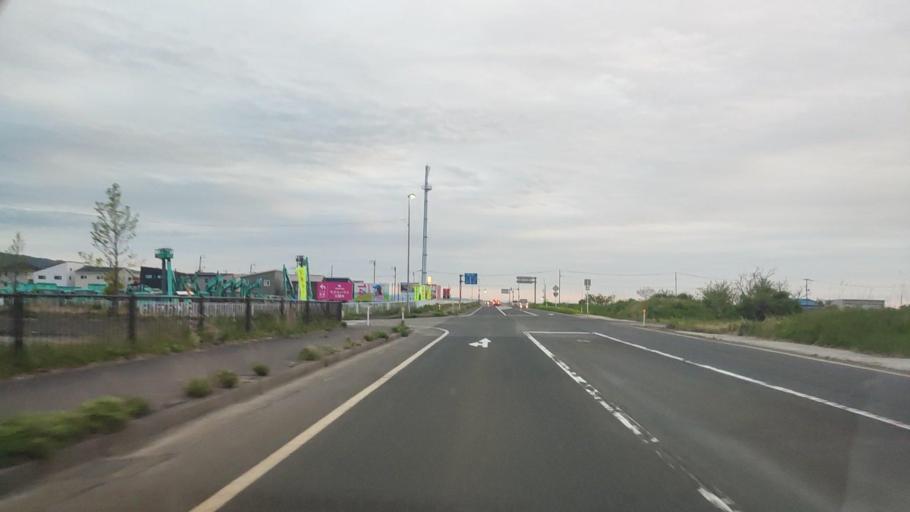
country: JP
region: Niigata
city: Niitsu-honcho
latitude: 37.7532
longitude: 139.0893
